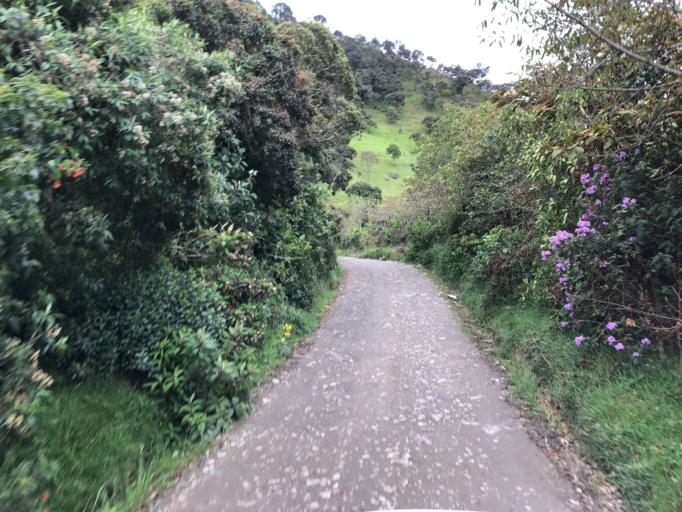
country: CO
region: Cauca
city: Totoro
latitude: 2.5018
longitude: -76.3573
